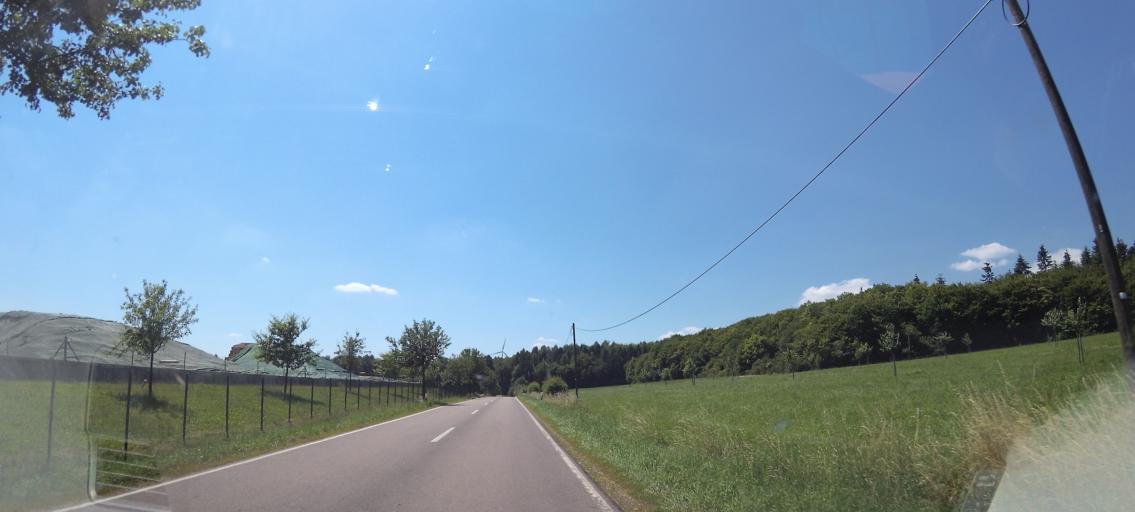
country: DE
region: Saarland
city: Mettlach
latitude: 49.4368
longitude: 6.5698
